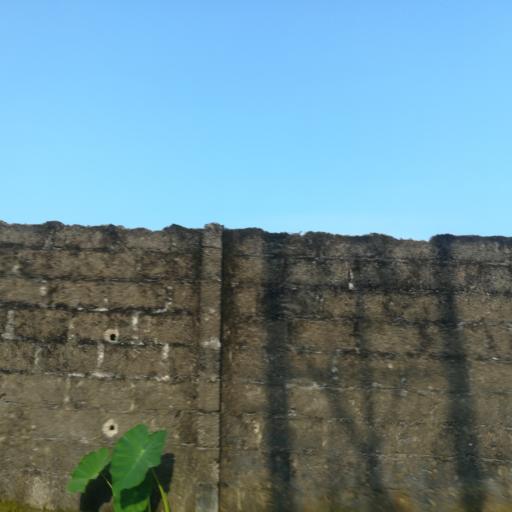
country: NG
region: Rivers
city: Port Harcourt
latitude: 4.8549
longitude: 6.9609
